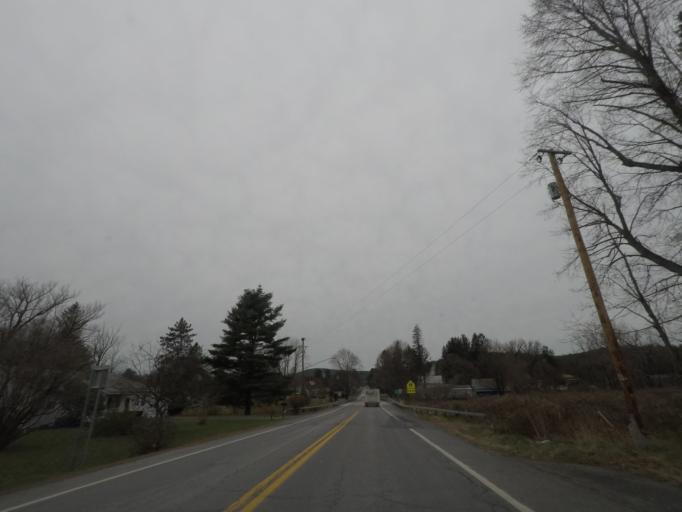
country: US
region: Massachusetts
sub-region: Berkshire County
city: Lanesborough
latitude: 42.5495
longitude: -73.3776
